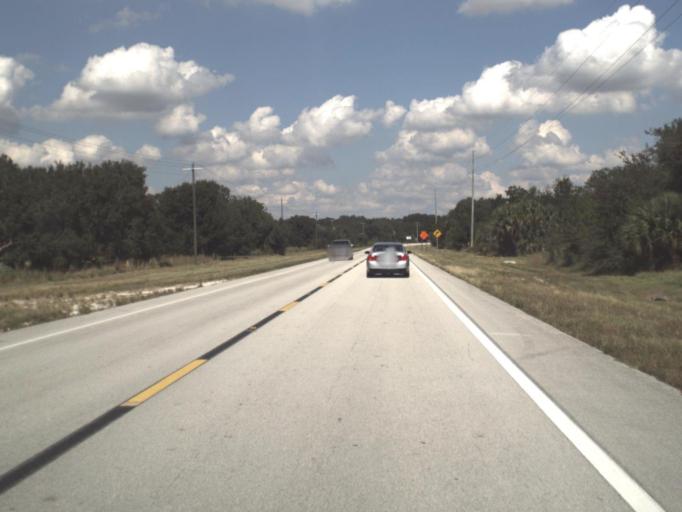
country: US
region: Florida
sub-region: Okeechobee County
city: Okeechobee
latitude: 27.3833
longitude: -81.0400
